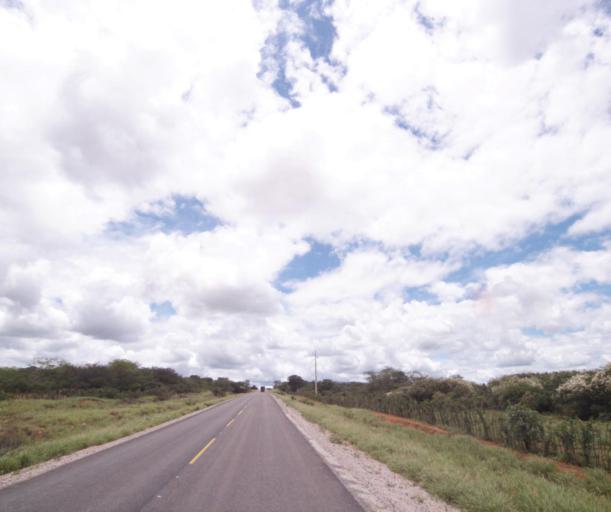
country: BR
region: Bahia
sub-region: Brumado
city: Brumado
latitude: -14.1507
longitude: -41.5006
